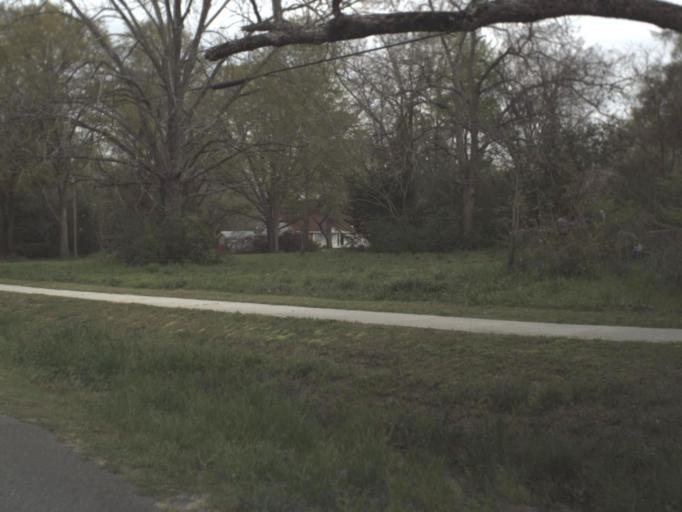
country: US
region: Alabama
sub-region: Geneva County
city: Hartford
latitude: 30.9853
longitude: -85.6463
